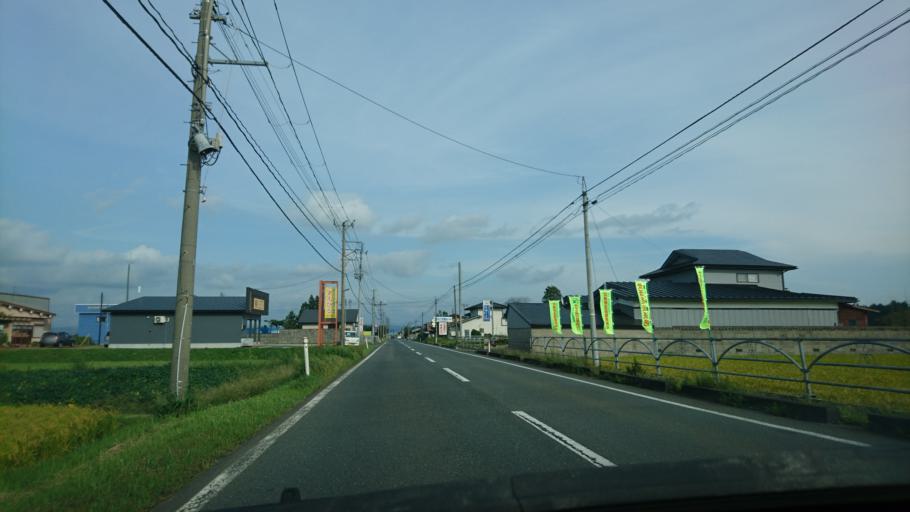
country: JP
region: Iwate
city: Kitakami
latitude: 39.3044
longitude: 141.0152
